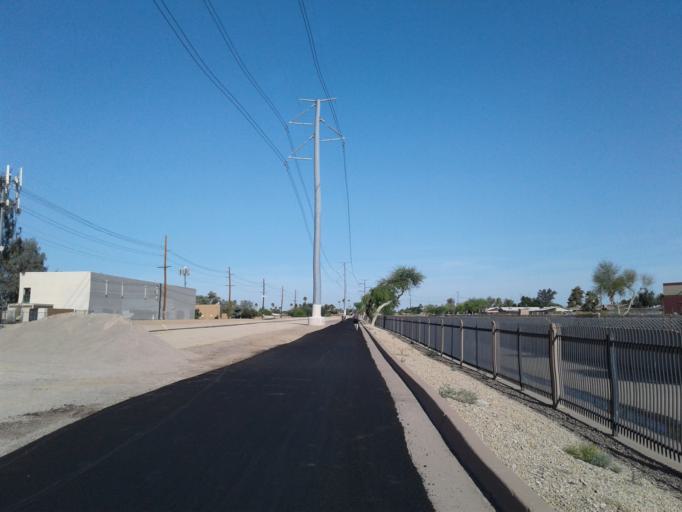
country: US
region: Arizona
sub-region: Maricopa County
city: Glendale
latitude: 33.5827
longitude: -112.1525
